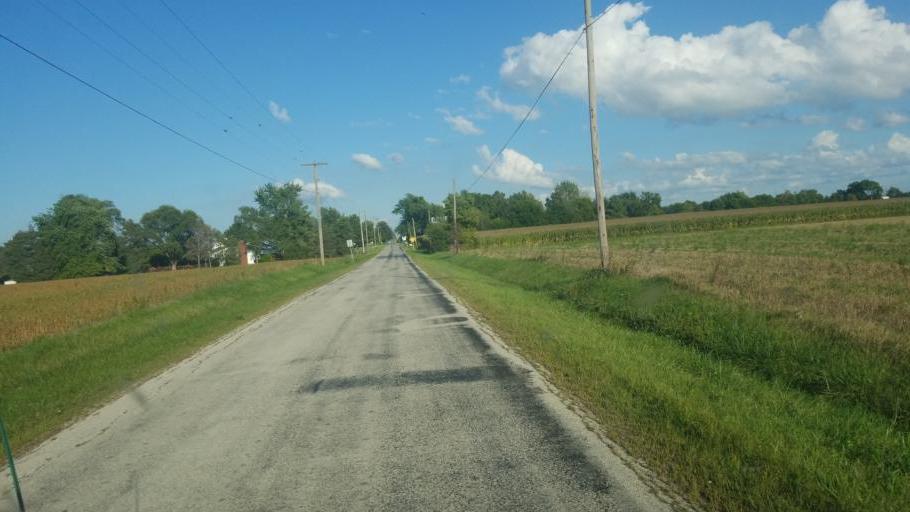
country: US
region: Ohio
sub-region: Hancock County
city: Arlington
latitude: 40.9355
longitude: -83.6005
